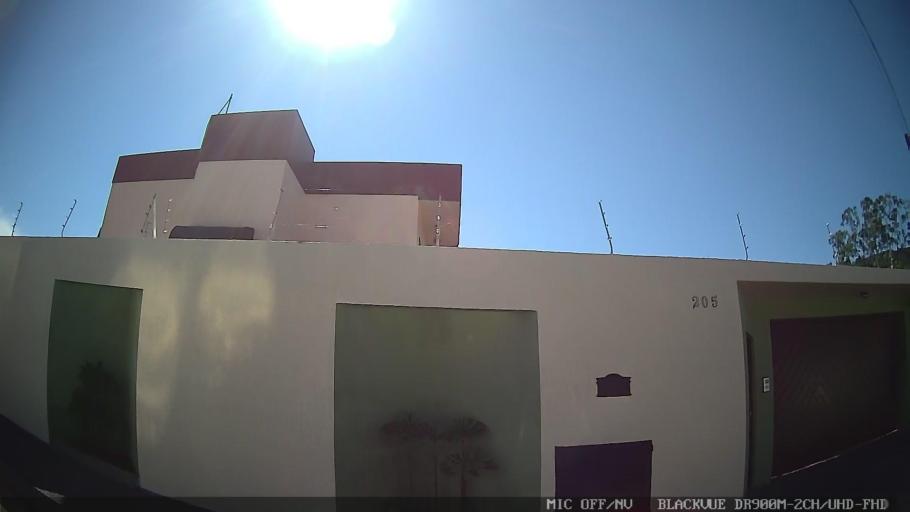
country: BR
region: Sao Paulo
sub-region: Iguape
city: Iguape
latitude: -24.7030
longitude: -47.5555
